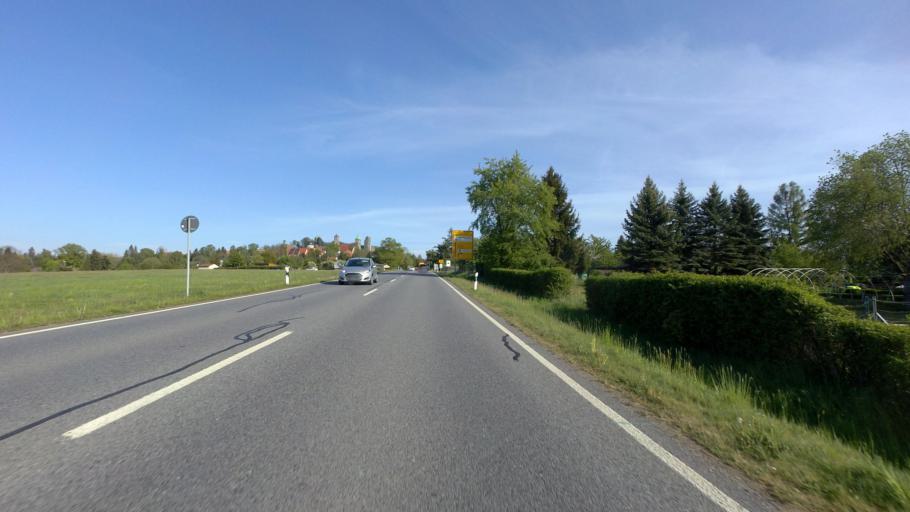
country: DE
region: Saxony
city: Stolpen
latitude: 51.0515
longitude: 14.0744
